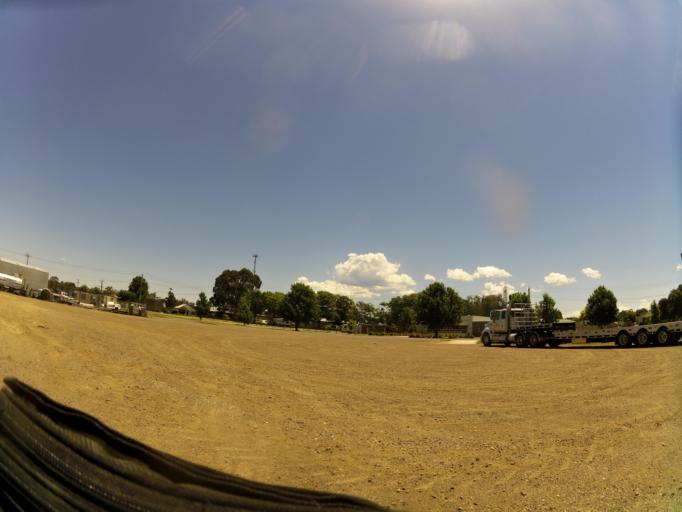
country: AU
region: Victoria
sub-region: Wellington
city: Sale
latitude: -37.9715
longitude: 146.9802
